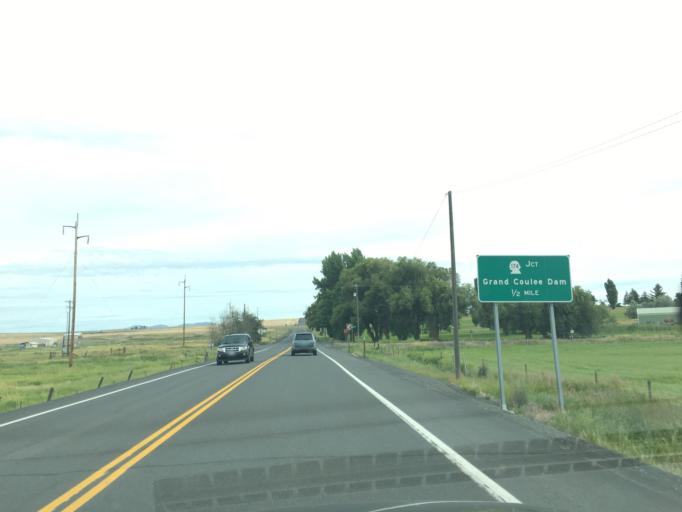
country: US
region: Washington
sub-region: Okanogan County
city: Coulee Dam
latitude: 47.7642
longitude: -118.7219
